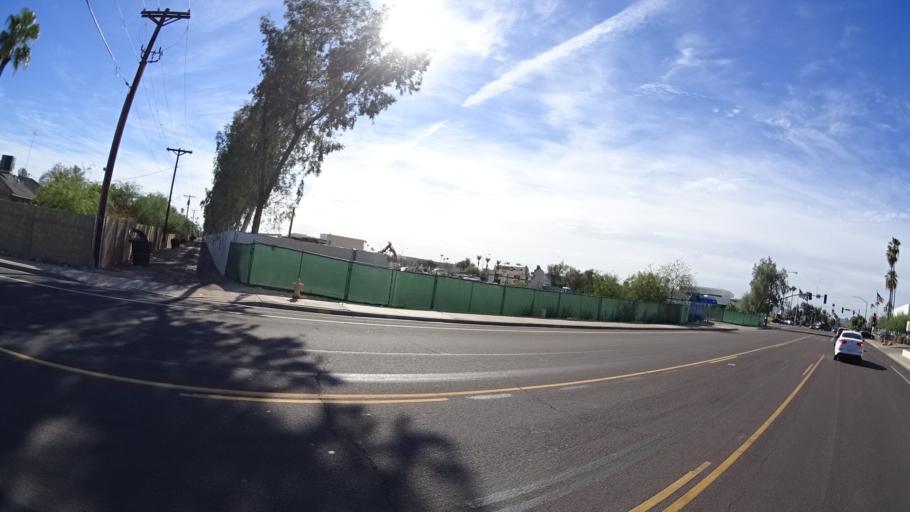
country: US
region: Arizona
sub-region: Maricopa County
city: Tempe Junction
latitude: 33.4666
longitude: -111.9349
